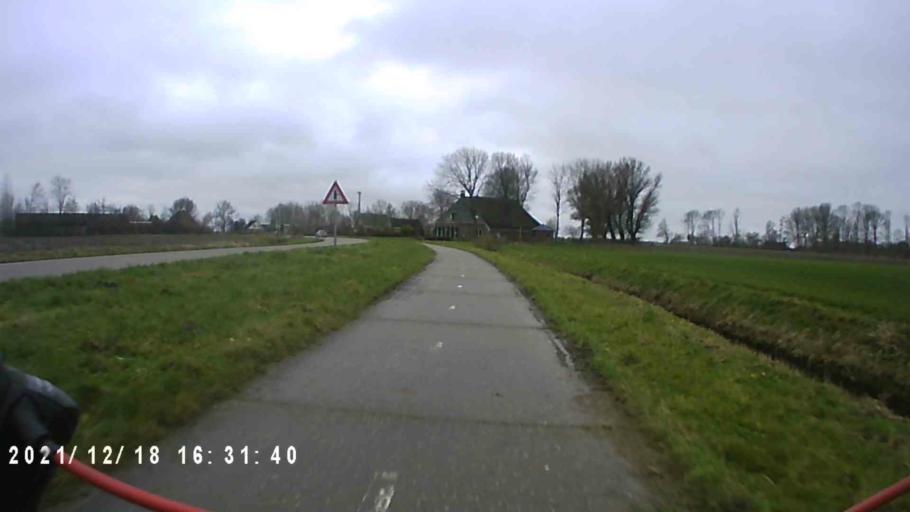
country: NL
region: Friesland
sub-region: Gemeente Dongeradeel
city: Dokkum
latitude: 53.3569
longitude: 6.0372
